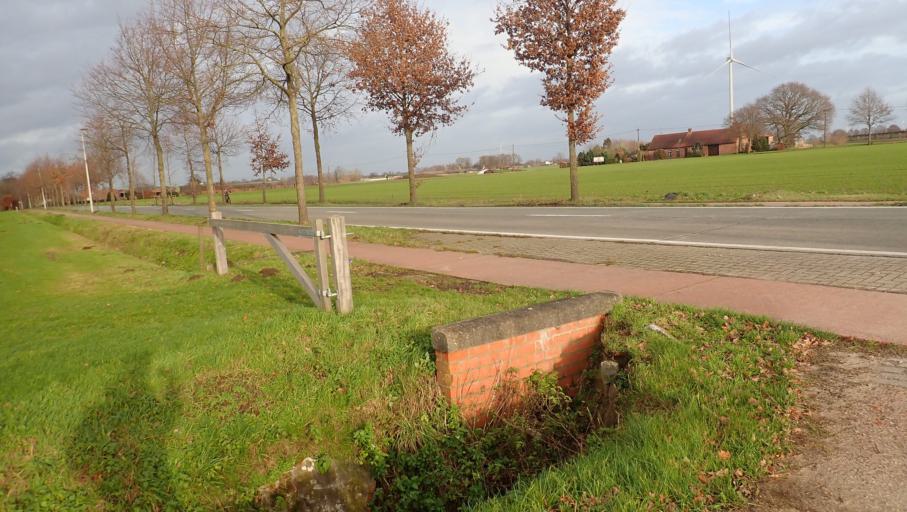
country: BE
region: Flanders
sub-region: Provincie Antwerpen
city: Brecht
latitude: 51.3769
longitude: 4.6449
